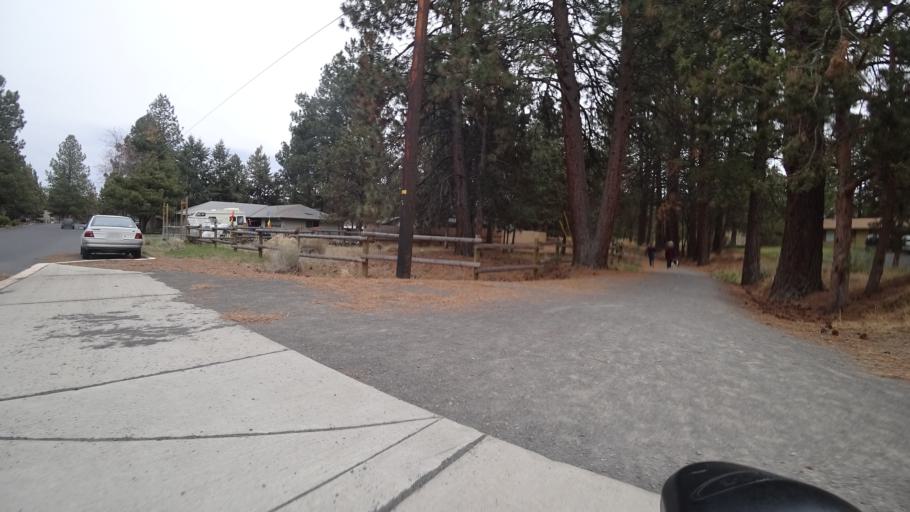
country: US
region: Oregon
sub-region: Deschutes County
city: Bend
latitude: 44.0460
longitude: -121.2791
